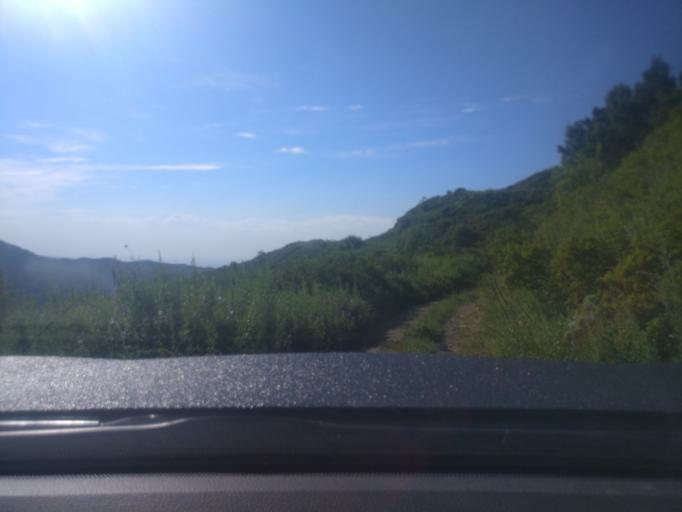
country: KZ
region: Almaty Qalasy
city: Almaty
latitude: 43.1142
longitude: 76.9303
